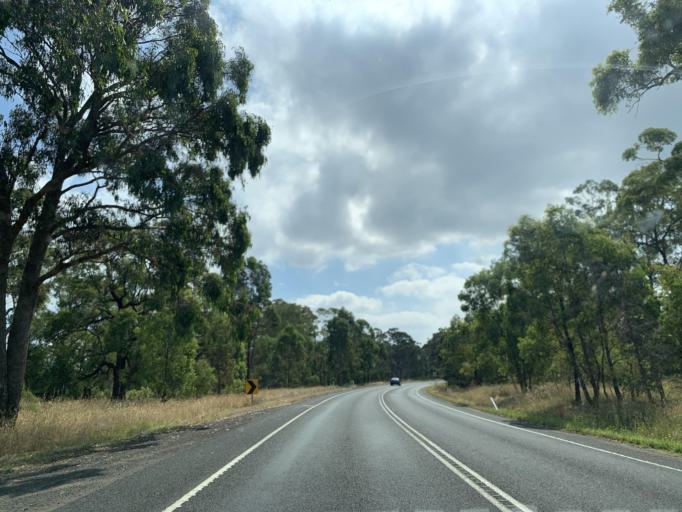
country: AU
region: Victoria
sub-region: Latrobe
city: Morwell
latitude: -38.2043
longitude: 146.4561
